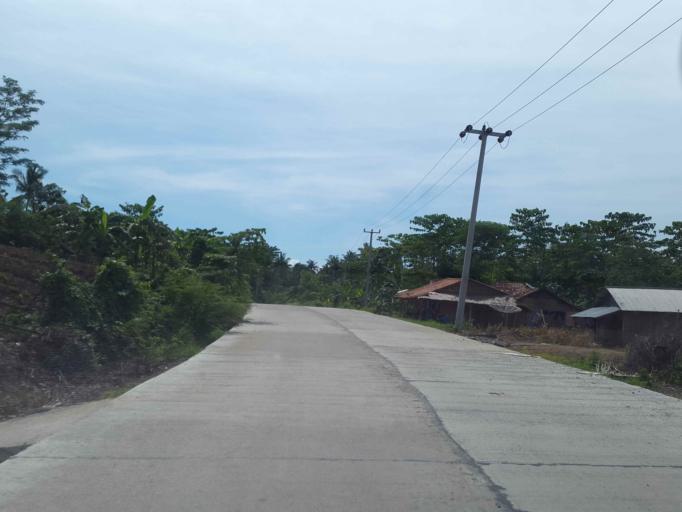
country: ID
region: Banten
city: Citeureup
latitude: -6.4980
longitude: 105.6514
